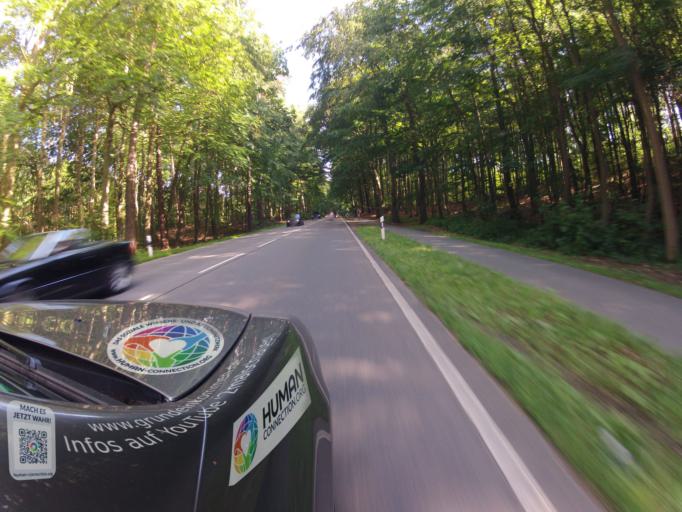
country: DE
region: Mecklenburg-Vorpommern
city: Loddin
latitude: 54.0074
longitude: 14.0578
